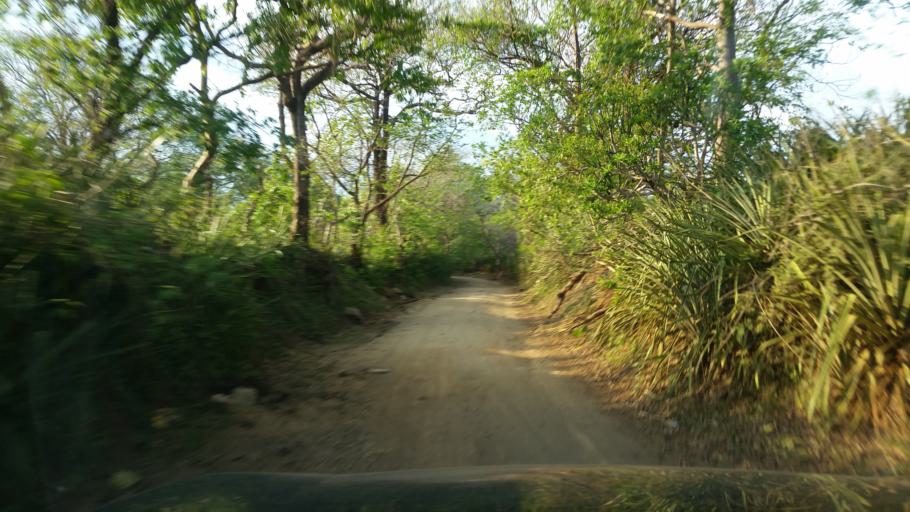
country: NI
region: Managua
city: Masachapa
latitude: 11.7945
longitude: -86.4701
